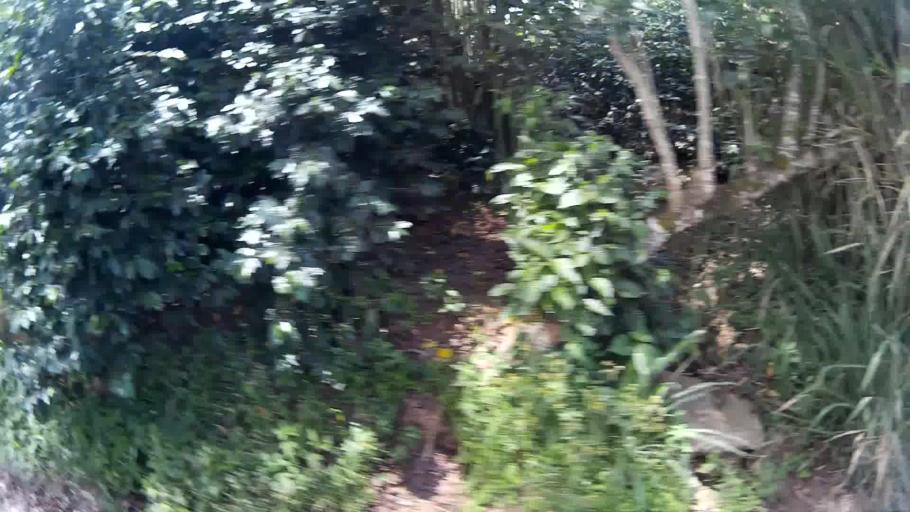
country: CO
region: Caldas
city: Belalcazar
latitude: 4.9562
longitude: -75.8298
